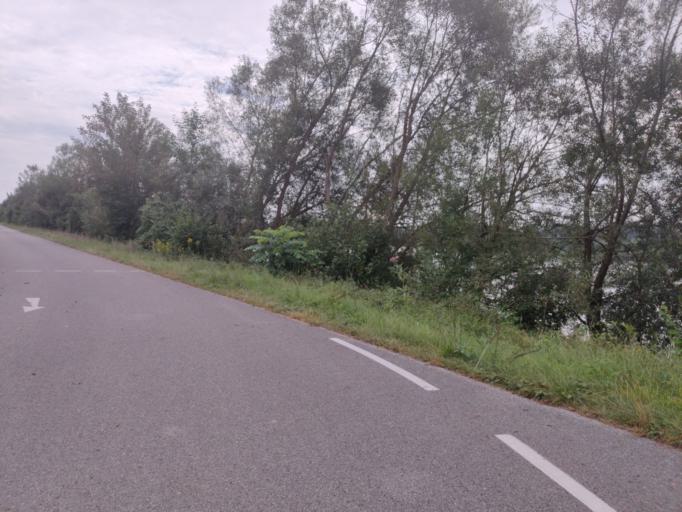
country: AT
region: Upper Austria
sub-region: Politischer Bezirk Perg
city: Perg
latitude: 48.2033
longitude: 14.6062
